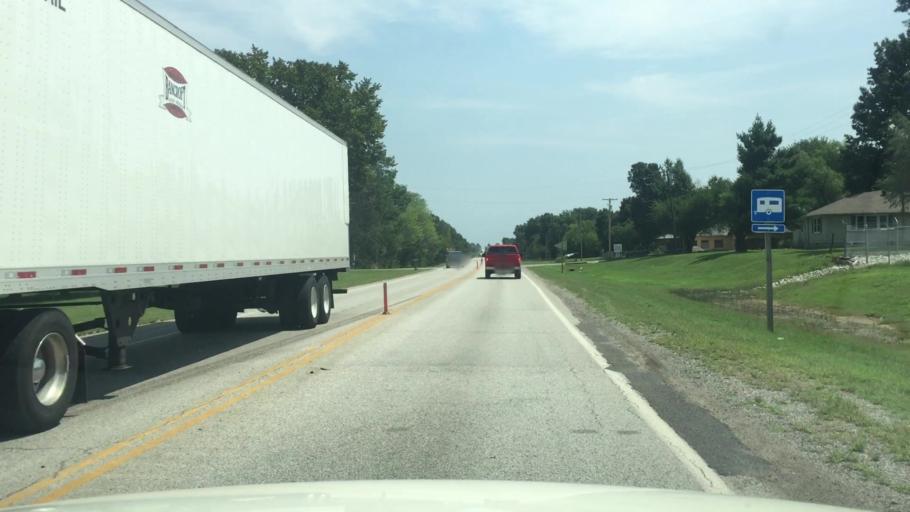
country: US
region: Kansas
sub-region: Cherokee County
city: Columbus
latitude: 37.1781
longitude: -94.8280
